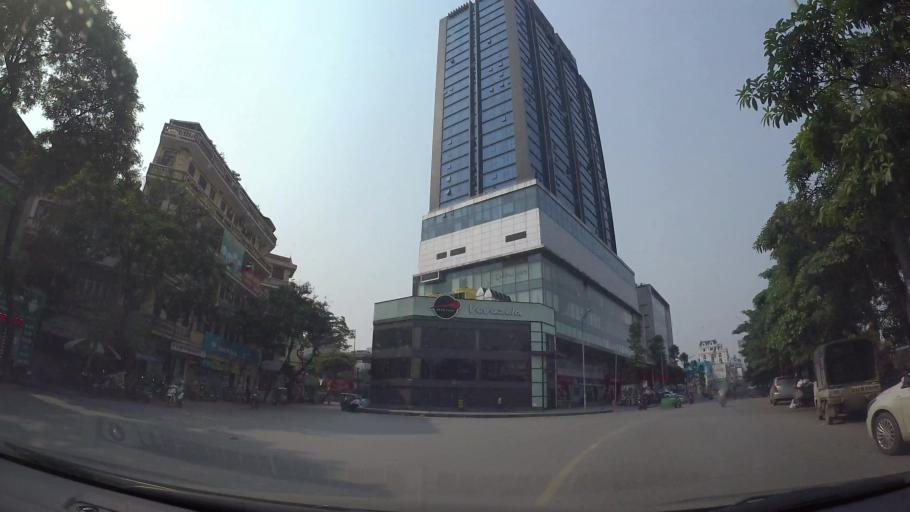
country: VN
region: Ha Noi
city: Dong Da
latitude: 20.9987
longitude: 105.8286
